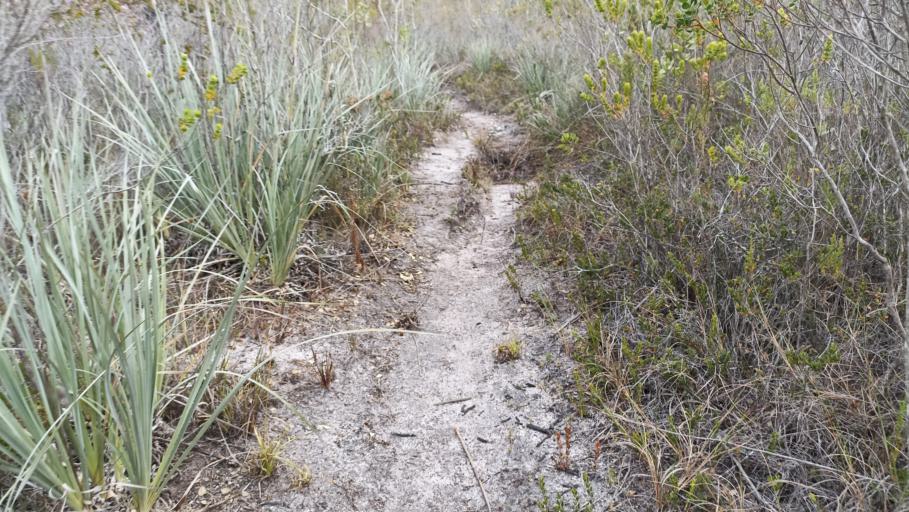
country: BR
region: Bahia
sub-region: Andarai
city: Vera Cruz
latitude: -12.9937
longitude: -41.3779
